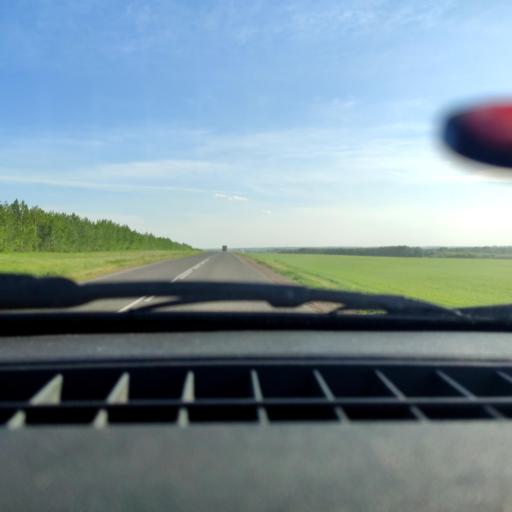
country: RU
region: Bashkortostan
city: Avdon
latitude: 54.4572
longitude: 55.8527
